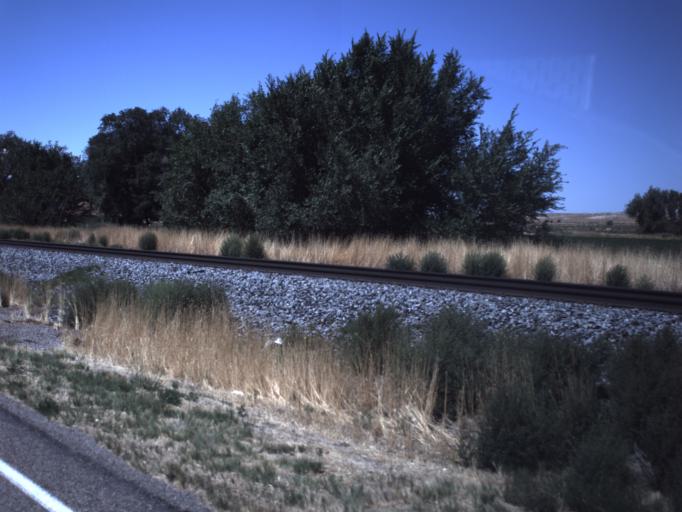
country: US
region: Utah
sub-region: Millard County
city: Delta
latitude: 39.5352
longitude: -112.2812
